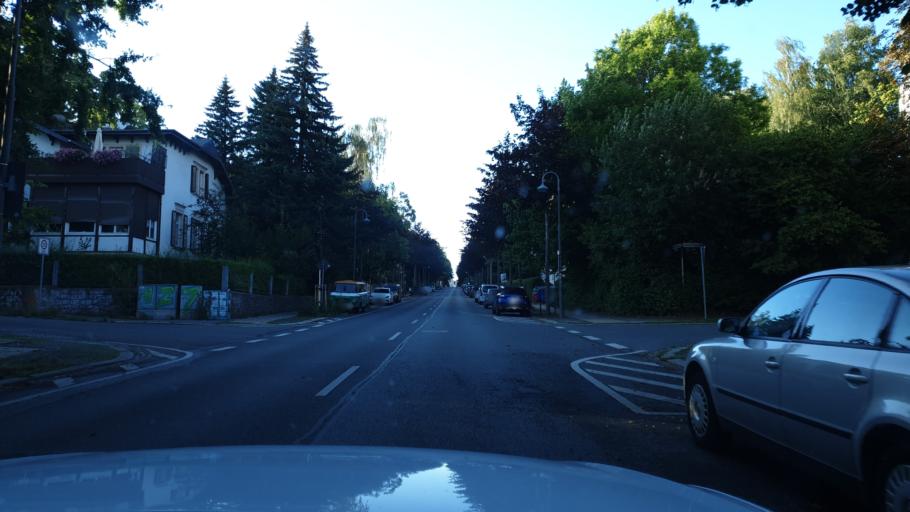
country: DE
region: Saxony
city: Chemnitz
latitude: 50.8277
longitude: 12.9040
